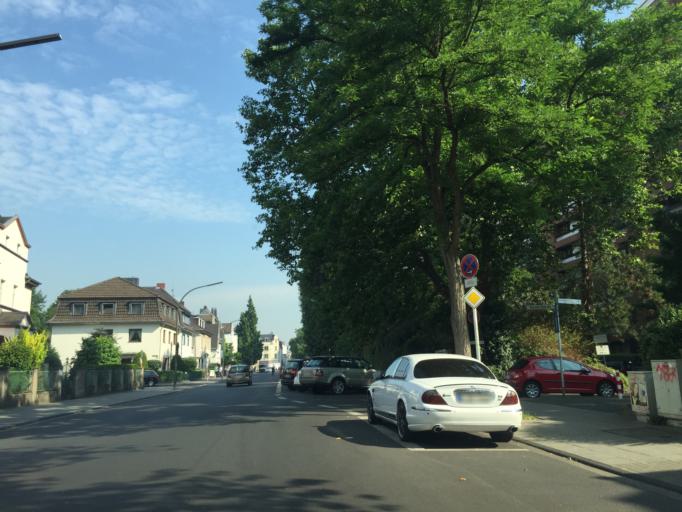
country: DE
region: North Rhine-Westphalia
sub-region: Regierungsbezirk Koln
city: Bayenthal
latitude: 50.9055
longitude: 6.9711
